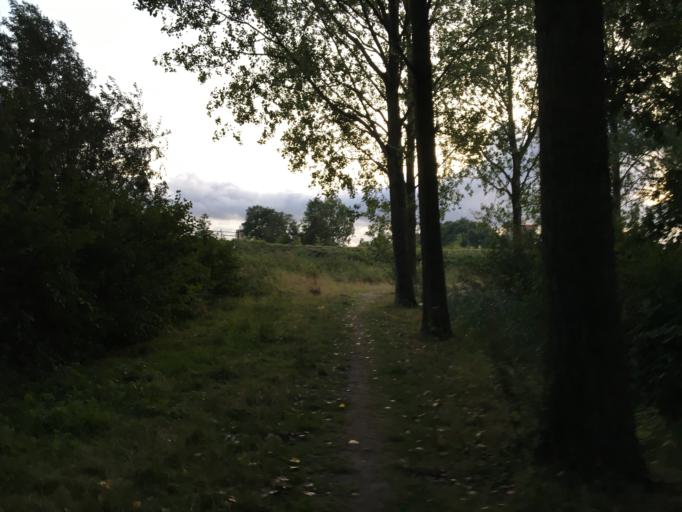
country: NL
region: Utrecht
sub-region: Gemeente Houten
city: Houten
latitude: 52.0256
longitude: 5.1517
